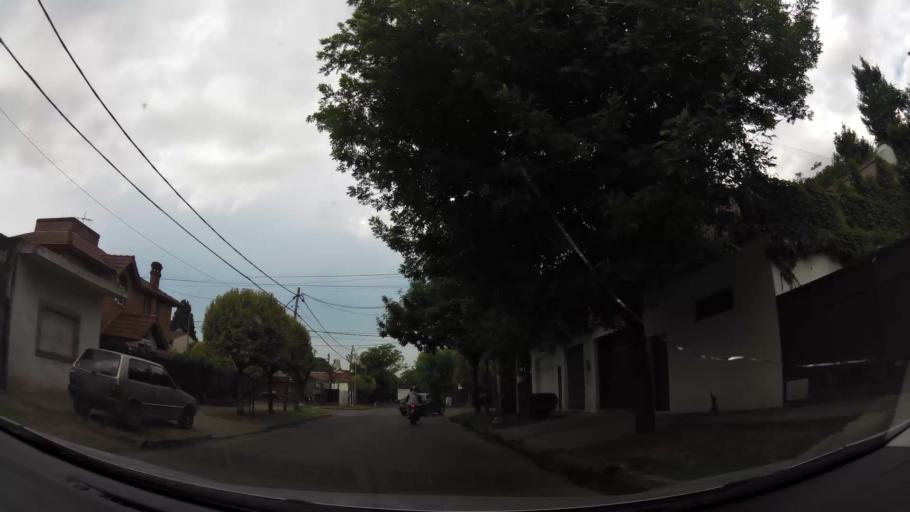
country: AR
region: Buenos Aires
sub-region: Partido de Tigre
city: Tigre
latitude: -34.4662
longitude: -58.6509
